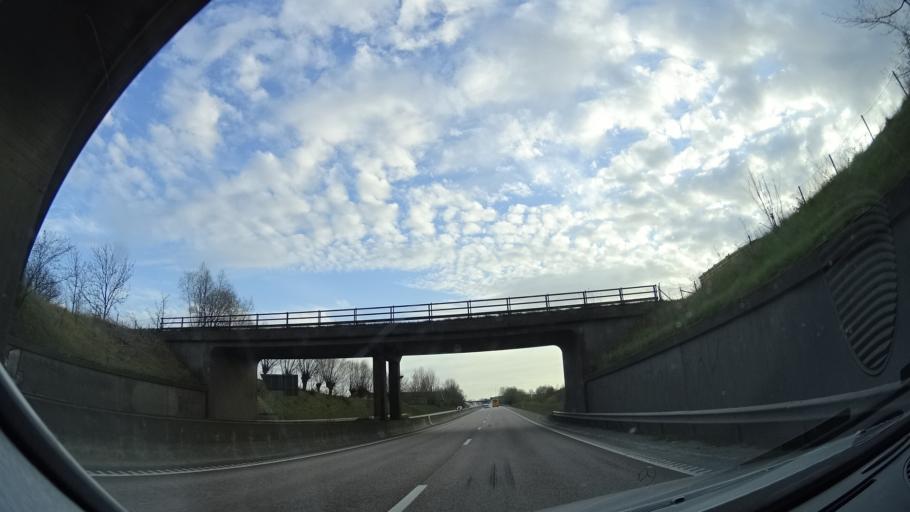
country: SE
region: Skane
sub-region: Lunds Kommun
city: Lund
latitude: 55.6830
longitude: 13.1909
